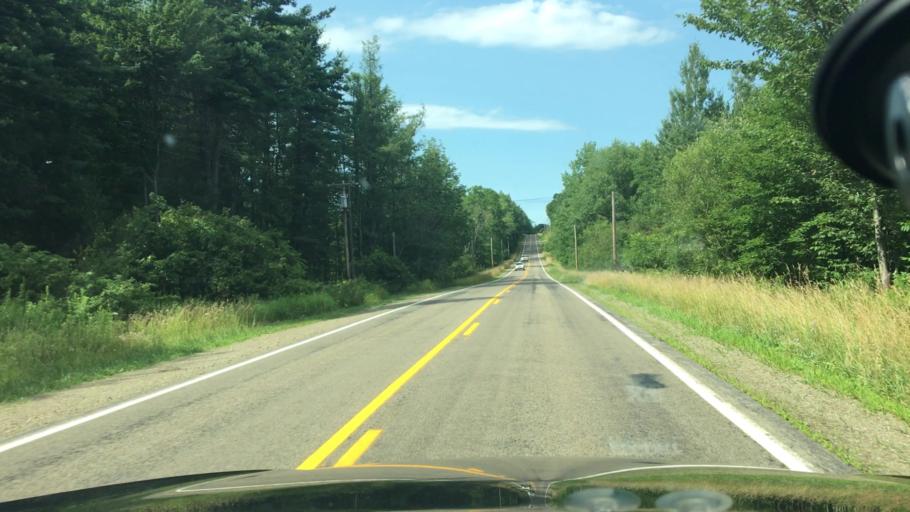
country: US
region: New York
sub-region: Chautauqua County
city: Lakewood
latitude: 42.2198
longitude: -79.3615
